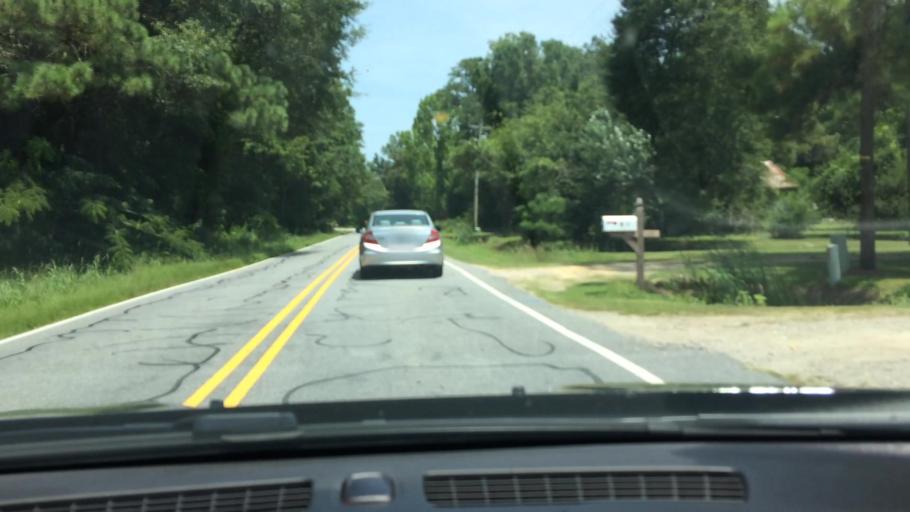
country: US
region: North Carolina
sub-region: Beaufort County
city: Washington
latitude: 35.5959
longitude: -77.1600
